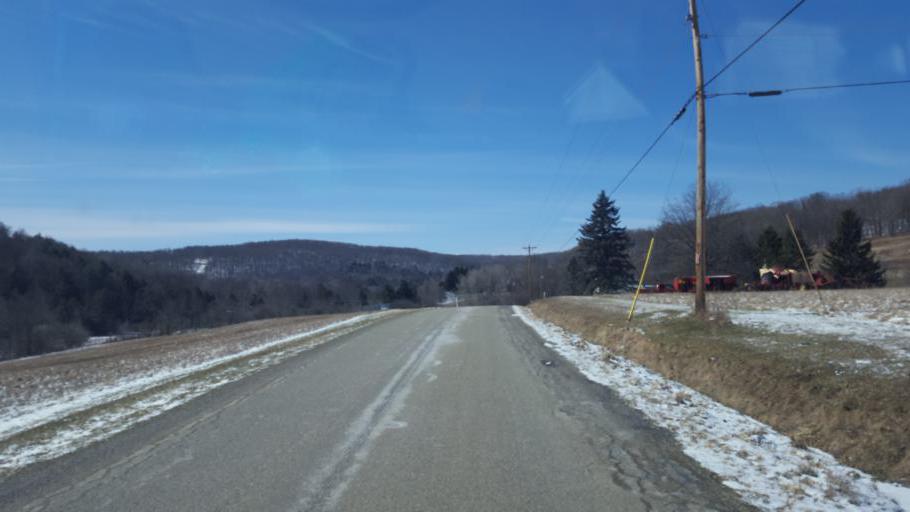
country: US
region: New York
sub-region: Allegany County
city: Andover
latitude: 41.9487
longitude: -77.8028
